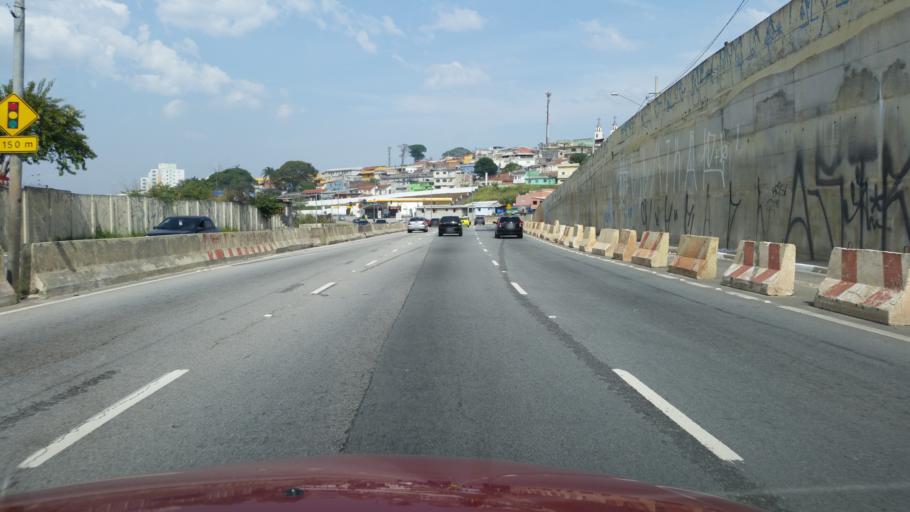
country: BR
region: Sao Paulo
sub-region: Ferraz De Vasconcelos
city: Ferraz de Vasconcelos
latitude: -23.5255
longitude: -46.4408
